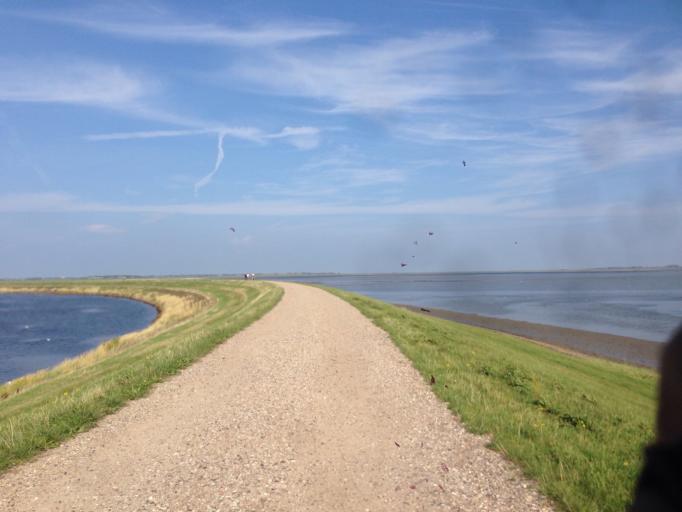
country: DE
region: Schleswig-Holstein
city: Tinnum
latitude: 54.8629
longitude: 8.3308
